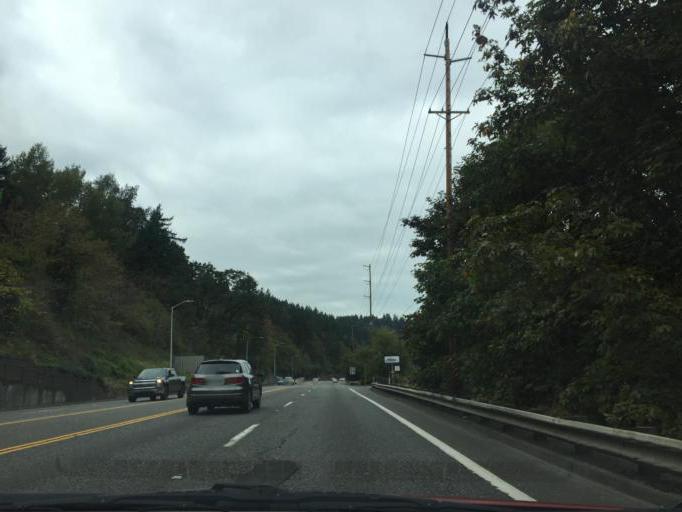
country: US
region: Oregon
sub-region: Washington County
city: West Haven
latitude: 45.5887
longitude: -122.7755
